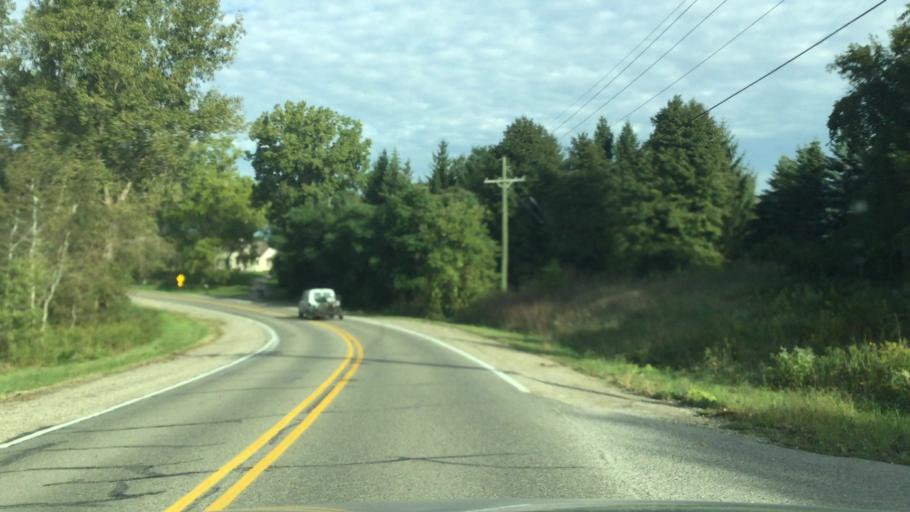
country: US
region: Michigan
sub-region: Livingston County
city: Brighton
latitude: 42.5350
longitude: -83.8680
